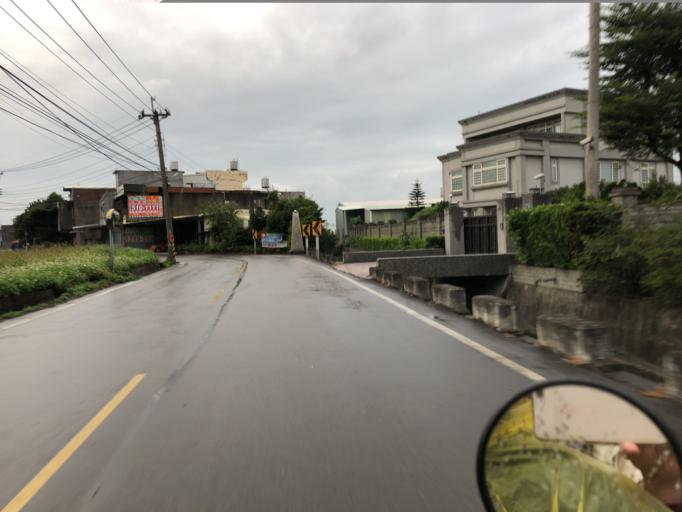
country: TW
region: Taiwan
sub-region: Hsinchu
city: Zhubei
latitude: 24.8463
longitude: 120.9898
